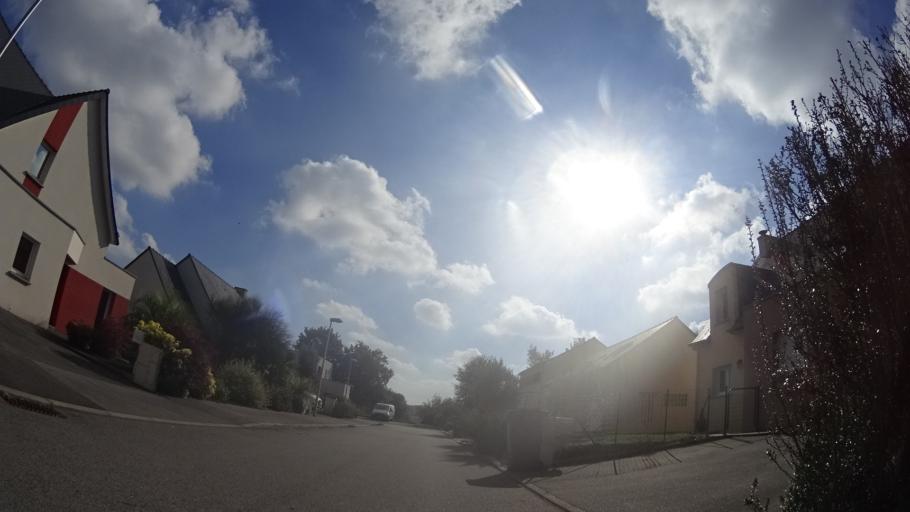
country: FR
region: Brittany
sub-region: Departement d'Ille-et-Vilaine
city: Geveze
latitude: 48.2232
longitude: -1.8038
